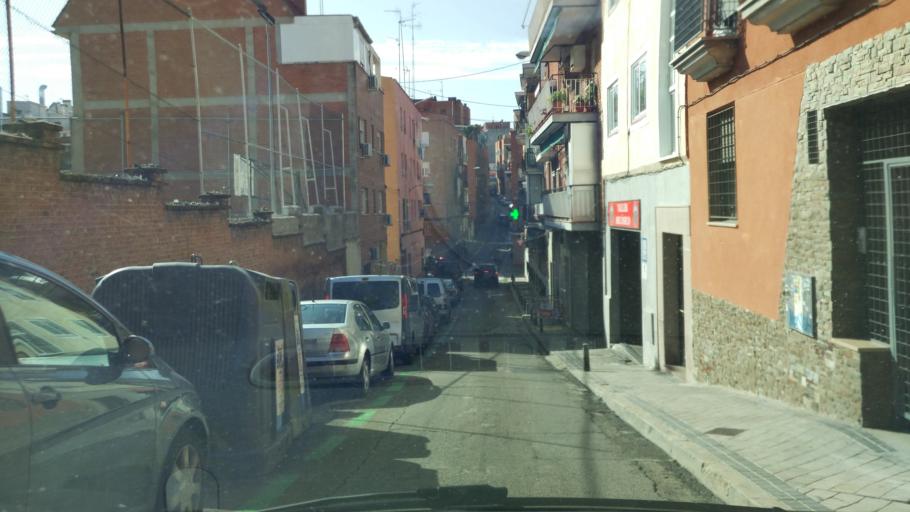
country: ES
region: Madrid
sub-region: Provincia de Madrid
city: Tetuan de las Victorias
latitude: 40.4696
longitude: -3.7007
